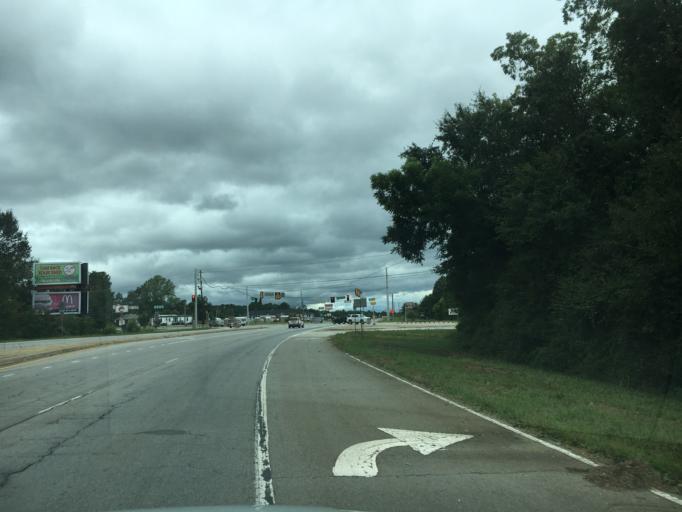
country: US
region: Georgia
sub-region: Wilkes County
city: Washington
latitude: 33.7252
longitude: -82.7146
